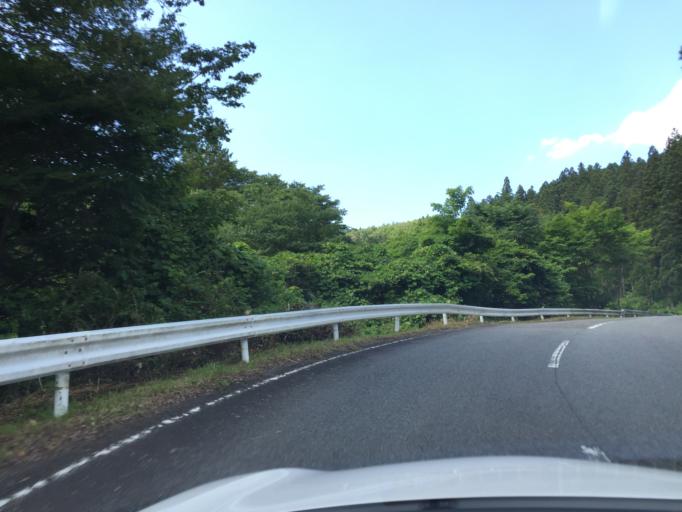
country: JP
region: Fukushima
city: Ishikawa
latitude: 37.1229
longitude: 140.6431
